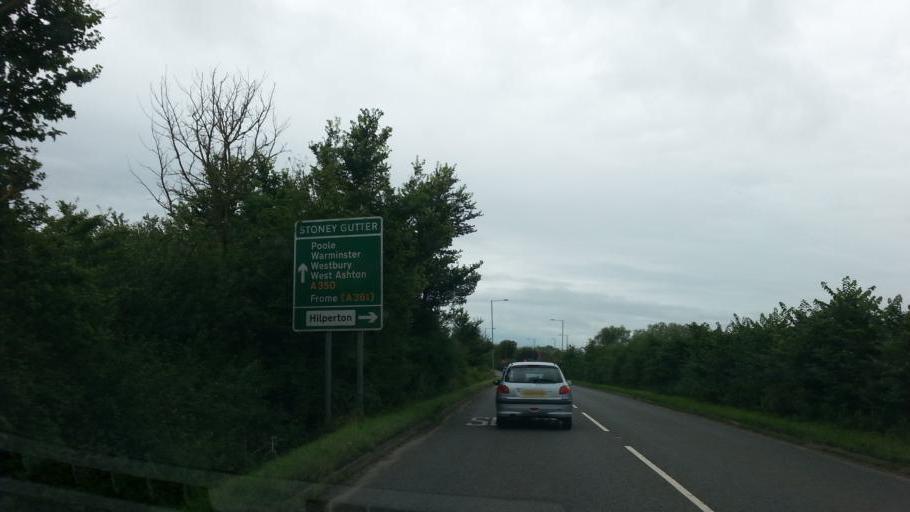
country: GB
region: England
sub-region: Wiltshire
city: Holt
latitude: 51.3235
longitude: -2.1570
